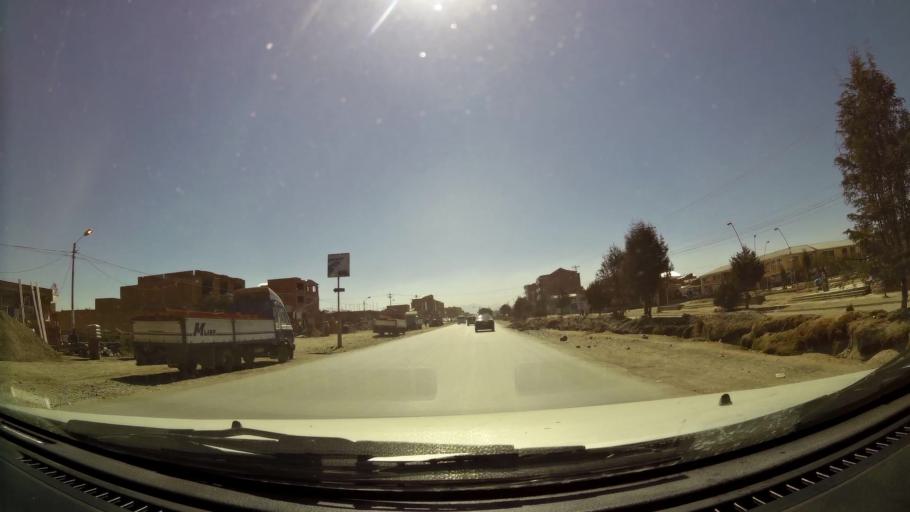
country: BO
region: La Paz
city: La Paz
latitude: -16.5684
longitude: -68.2219
